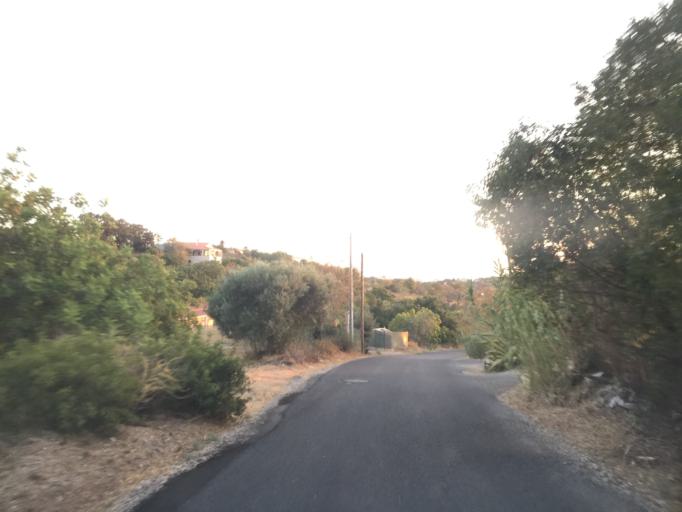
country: PT
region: Faro
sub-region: Loule
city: Almancil
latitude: 37.1062
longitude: -8.0082
